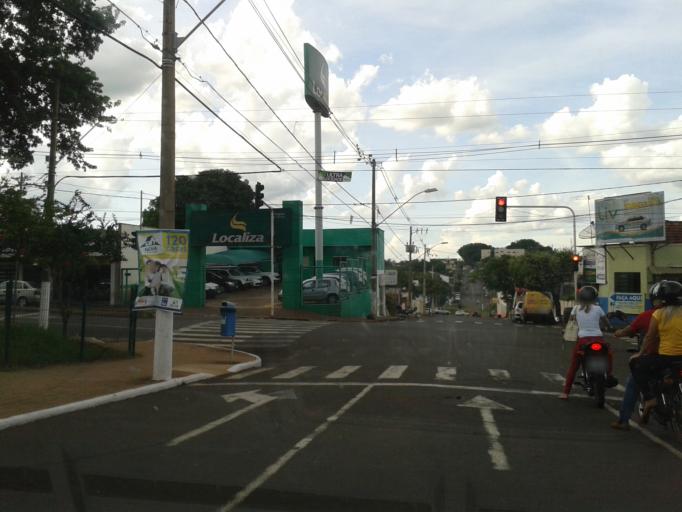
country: BR
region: Minas Gerais
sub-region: Ituiutaba
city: Ituiutaba
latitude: -18.9738
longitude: -49.4548
